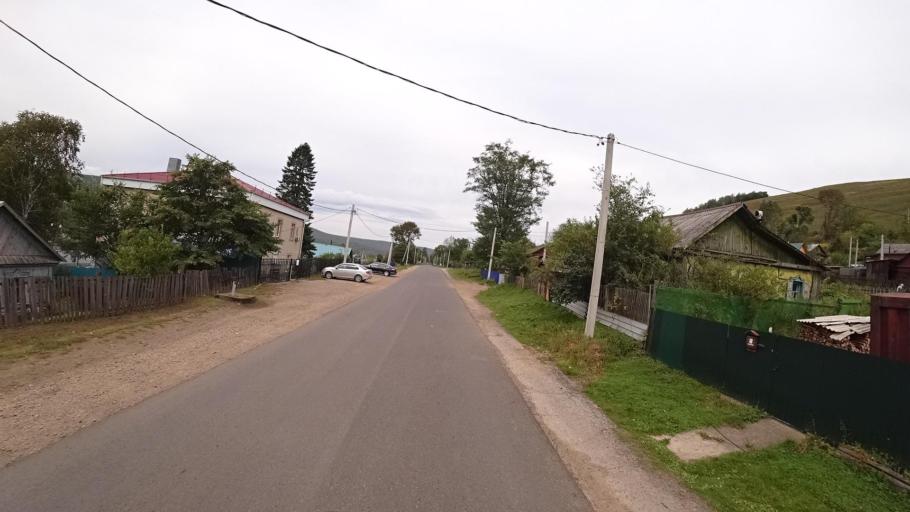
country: RU
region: Jewish Autonomous Oblast
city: Khingansk
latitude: 49.0225
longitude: 131.0596
